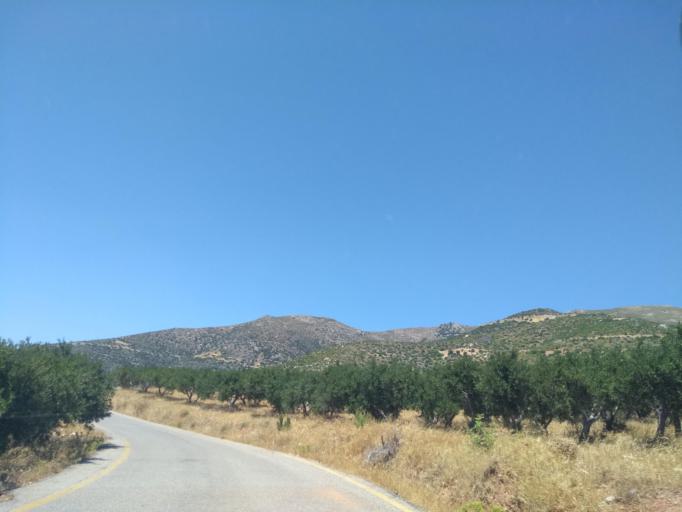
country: GR
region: Crete
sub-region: Nomos Chanias
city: Vryses
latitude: 35.3592
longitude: 23.5460
